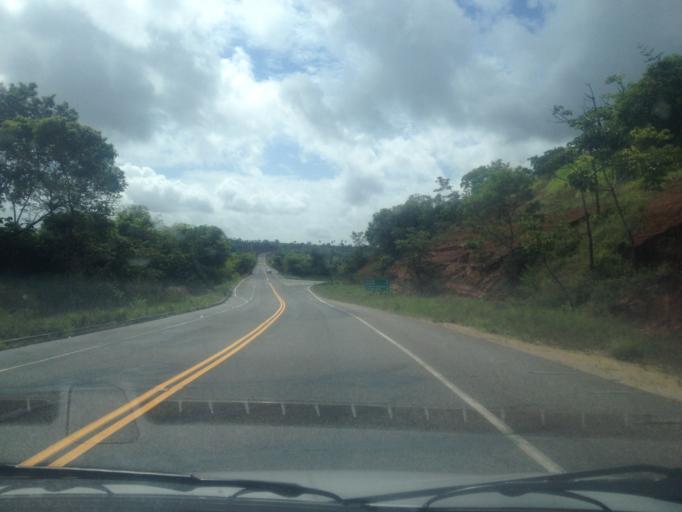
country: BR
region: Bahia
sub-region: Conde
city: Conde
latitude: -12.0649
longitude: -37.7454
